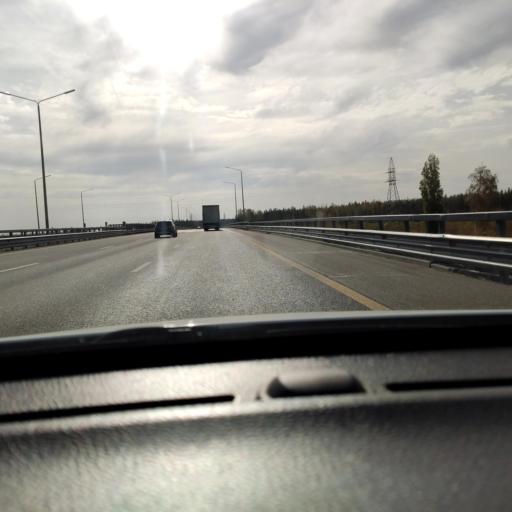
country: RU
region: Voronezj
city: Somovo
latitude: 51.7362
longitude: 39.3091
